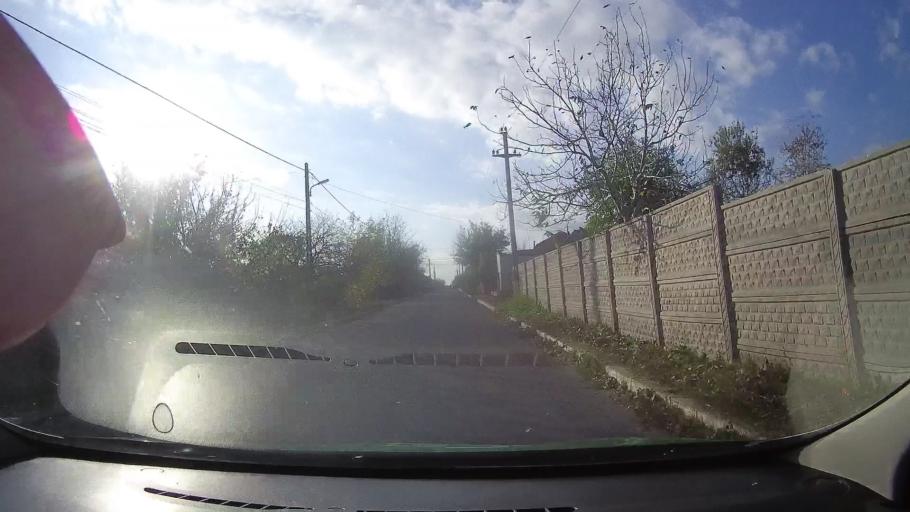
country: RO
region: Constanta
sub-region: Comuna Lumina
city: Lumina
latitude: 44.2876
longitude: 28.5641
